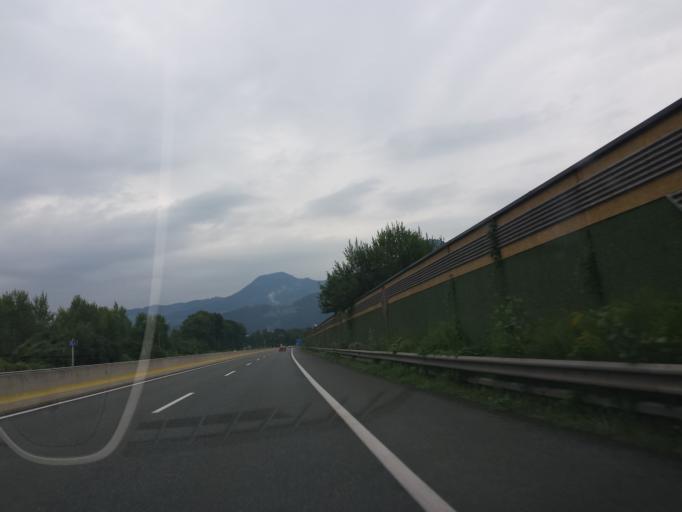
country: AT
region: Styria
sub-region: Politischer Bezirk Graz-Umgebung
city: Frohnleiten
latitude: 47.2535
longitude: 15.3171
